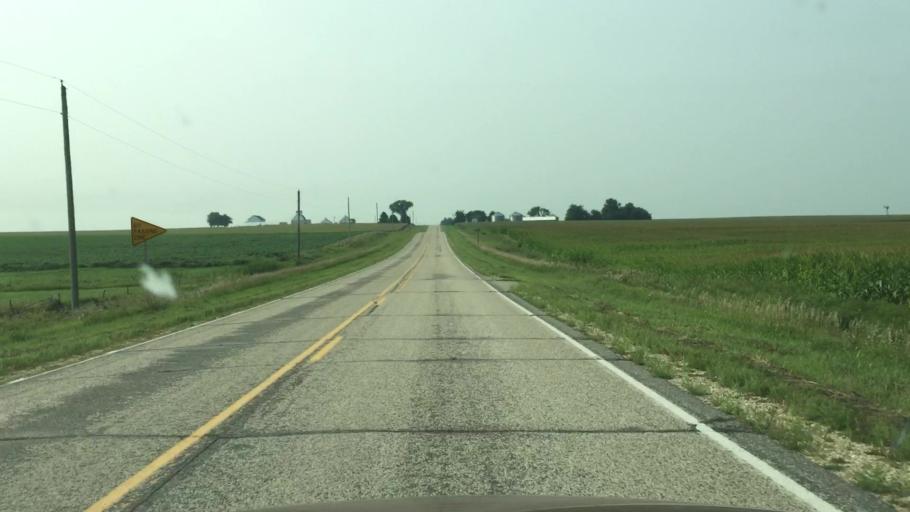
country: US
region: Iowa
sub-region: O'Brien County
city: Sheldon
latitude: 43.2756
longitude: -95.7829
